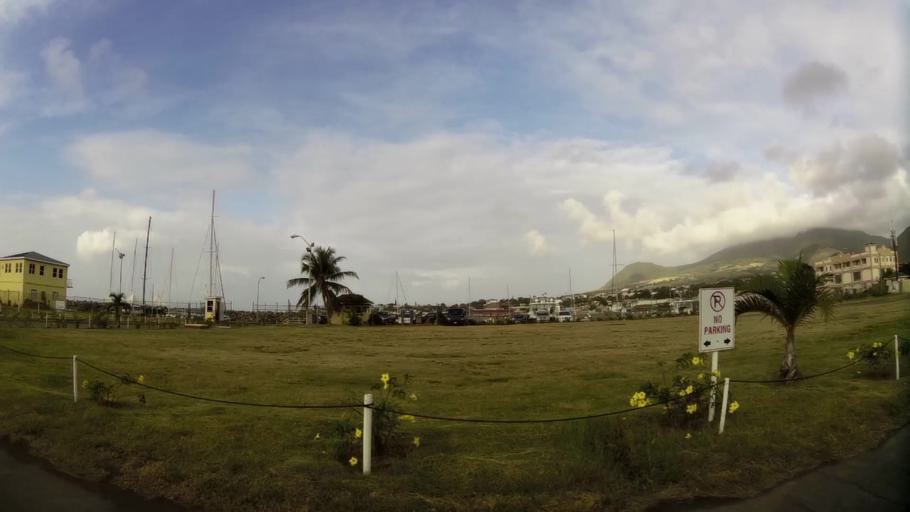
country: KN
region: Saint George Basseterre
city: Basseterre
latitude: 17.2929
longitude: -62.7237
